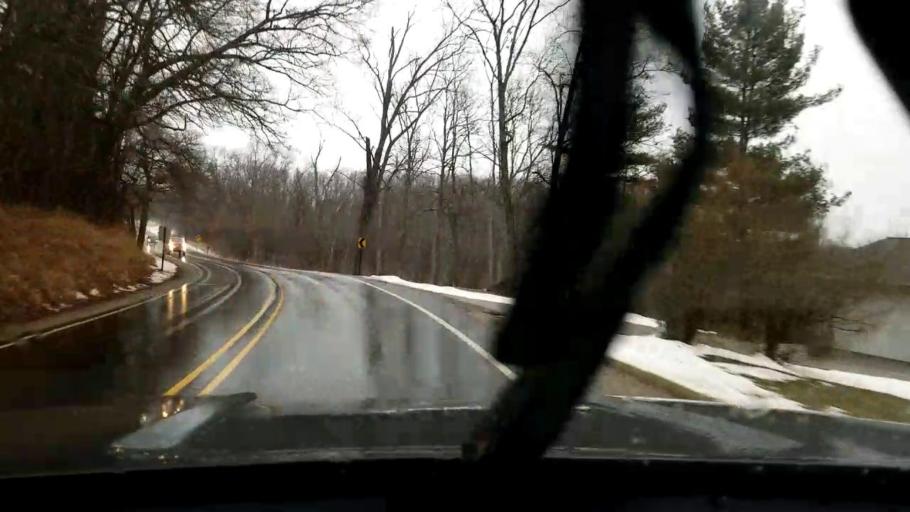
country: US
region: Michigan
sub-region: Jackson County
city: Michigan Center
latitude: 42.2853
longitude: -84.3288
